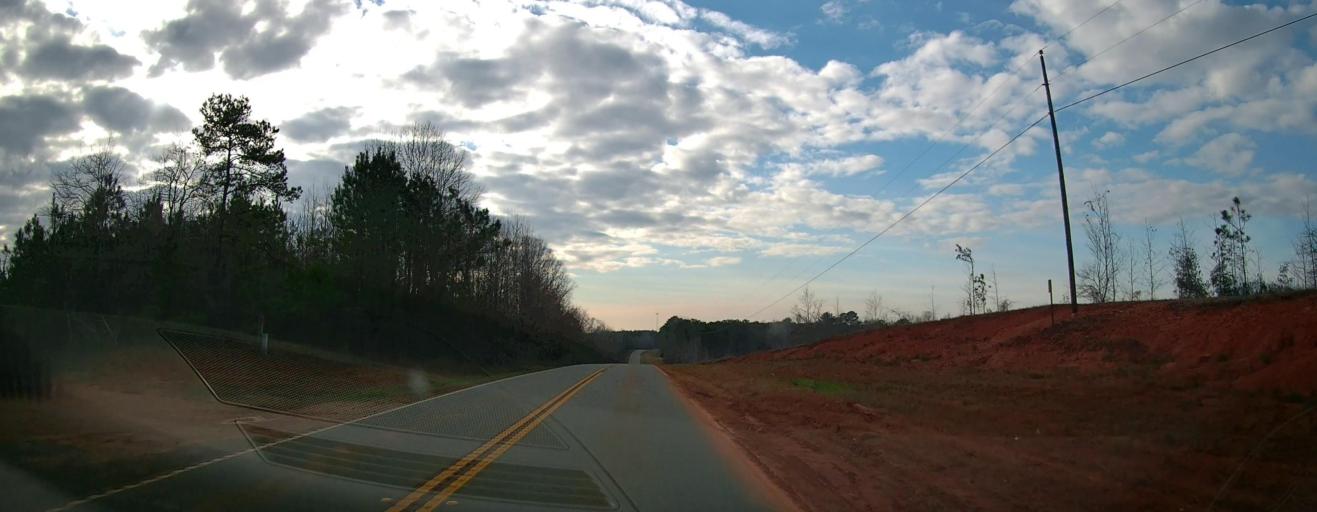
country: US
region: Georgia
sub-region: Harris County
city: Hamilton
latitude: 32.6862
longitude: -84.7720
